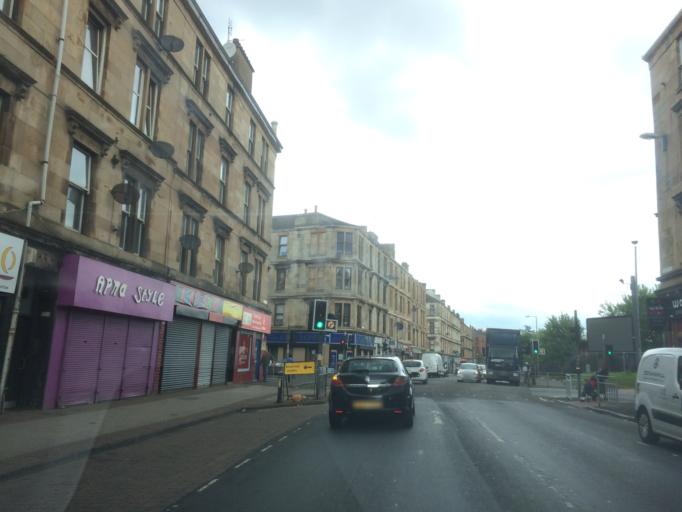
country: GB
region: Scotland
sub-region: Glasgow City
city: Glasgow
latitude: 55.8364
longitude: -4.2570
